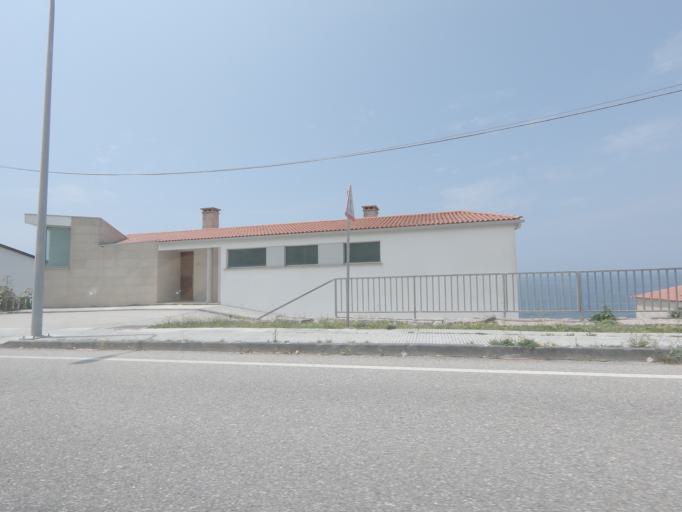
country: ES
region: Galicia
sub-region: Provincia de Pontevedra
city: A Guarda
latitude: 41.8927
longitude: -8.8772
